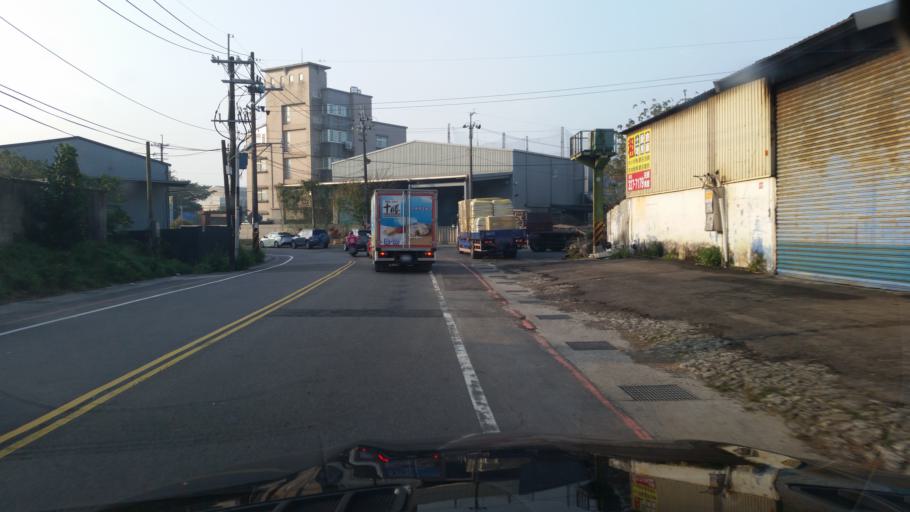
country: TW
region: Taiwan
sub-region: Taoyuan
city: Taoyuan
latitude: 25.0583
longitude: 121.3569
